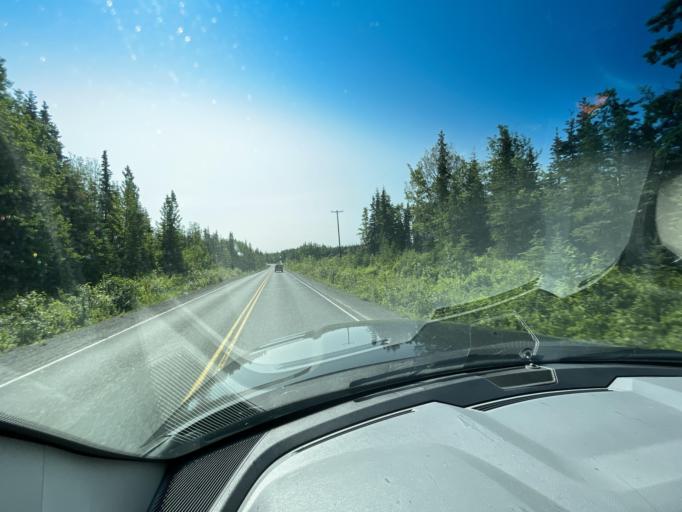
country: US
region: Alaska
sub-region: Kenai Peninsula Borough
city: Cohoe
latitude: 60.3030
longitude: -151.2852
